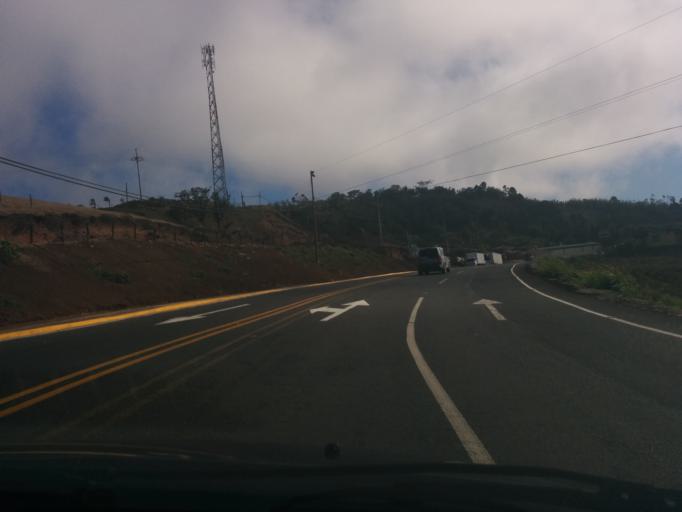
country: CR
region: Alajuela
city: San Rafael
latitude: 10.0665
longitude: -84.4995
